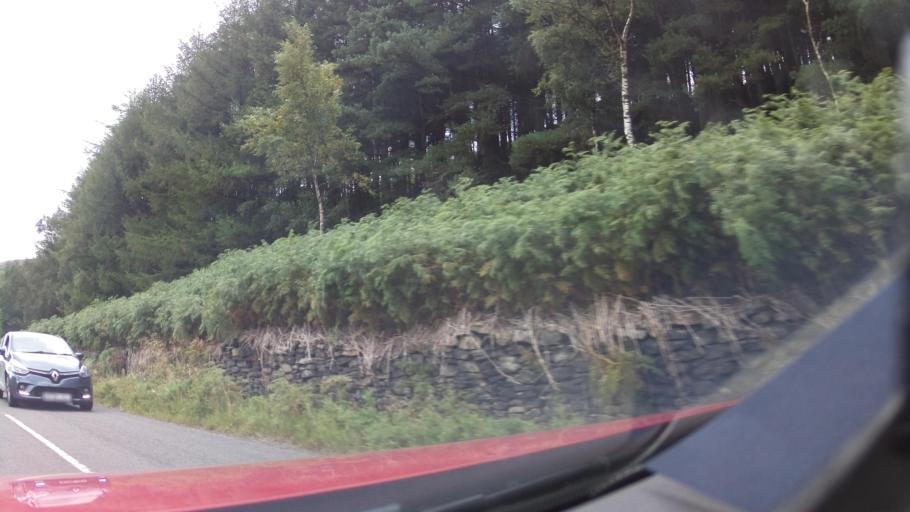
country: GB
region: England
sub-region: Kirklees
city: Meltham
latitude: 53.5015
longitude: -1.8567
